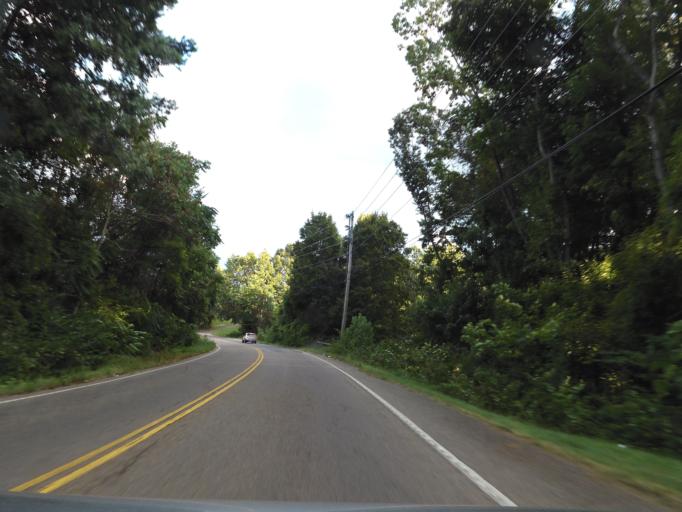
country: US
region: Tennessee
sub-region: Jefferson County
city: Jefferson City
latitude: 36.1276
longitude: -83.5192
